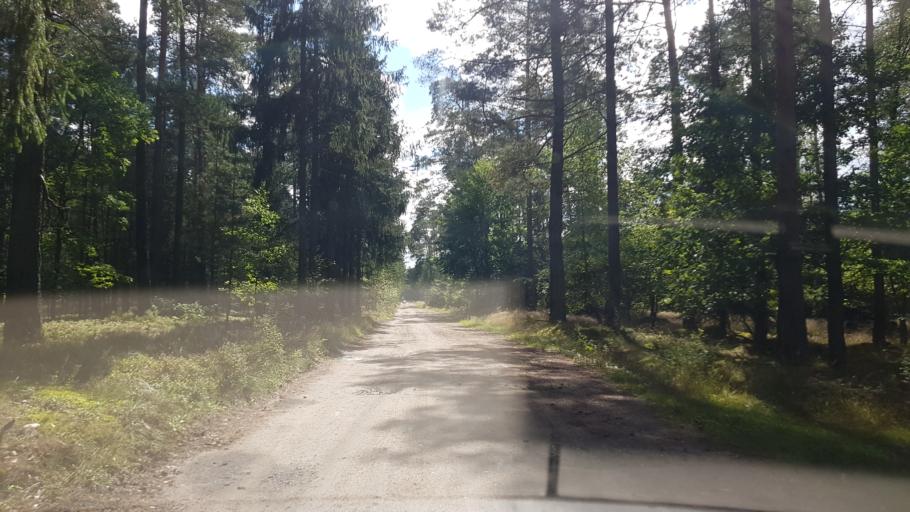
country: PL
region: West Pomeranian Voivodeship
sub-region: Powiat bialogardzki
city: Tychowo
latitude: 54.0184
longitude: 16.2992
